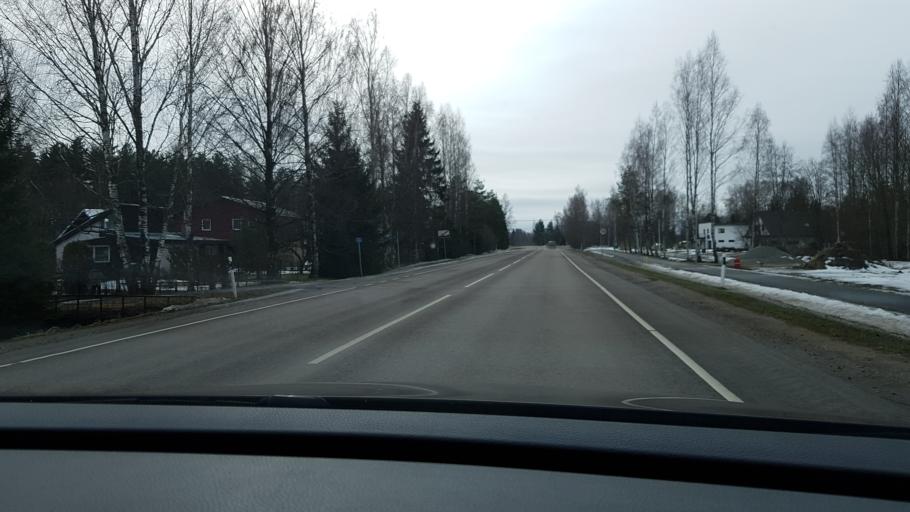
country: EE
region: Paernumaa
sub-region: Paikuse vald
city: Paikuse
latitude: 58.3942
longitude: 24.6449
